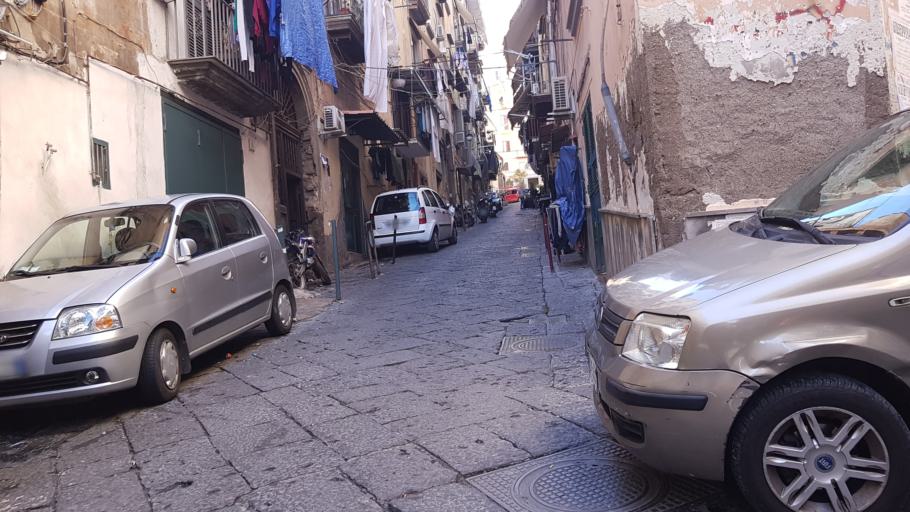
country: IT
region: Campania
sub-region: Provincia di Napoli
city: Napoli
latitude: 40.8394
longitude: 14.2457
